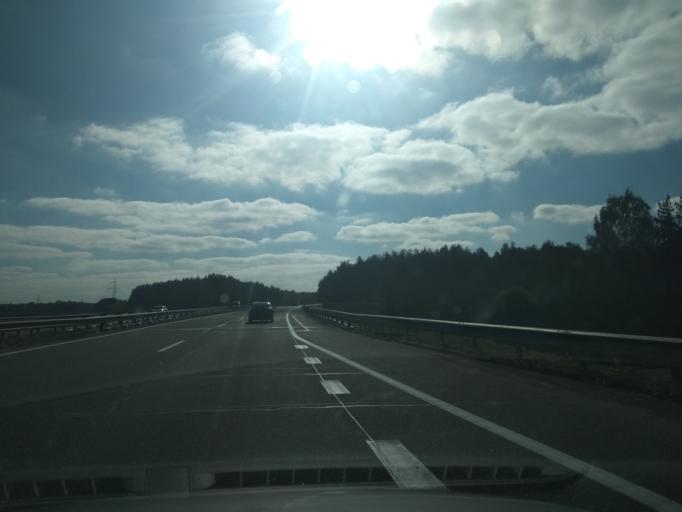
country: BY
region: Brest
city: Baranovichi
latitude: 53.0874
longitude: 25.8870
